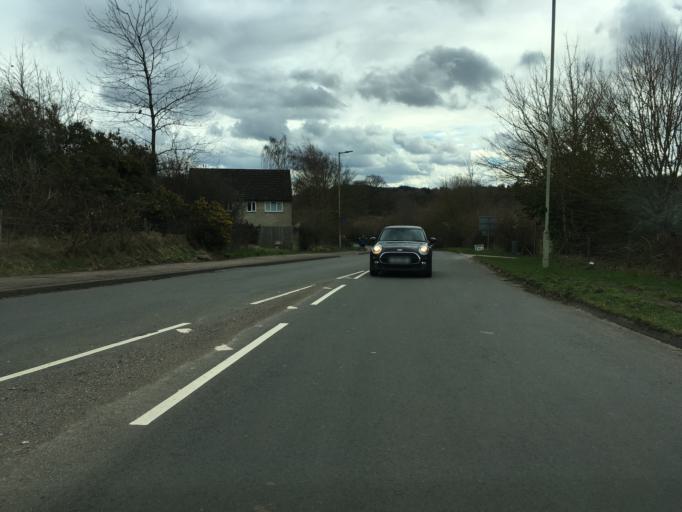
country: GB
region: England
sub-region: Gloucestershire
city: Cinderford
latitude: 51.8222
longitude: -2.5096
